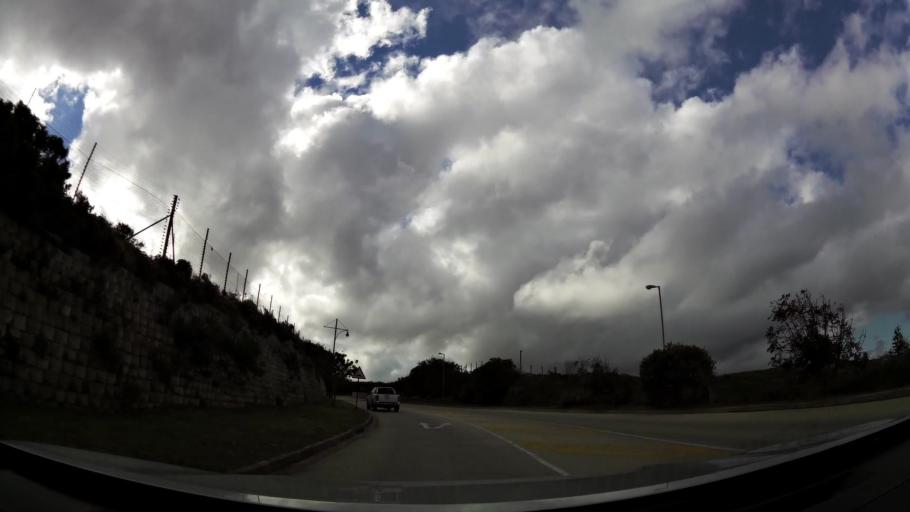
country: ZA
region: Western Cape
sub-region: Eden District Municipality
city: Knysna
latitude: -34.0726
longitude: 23.0871
